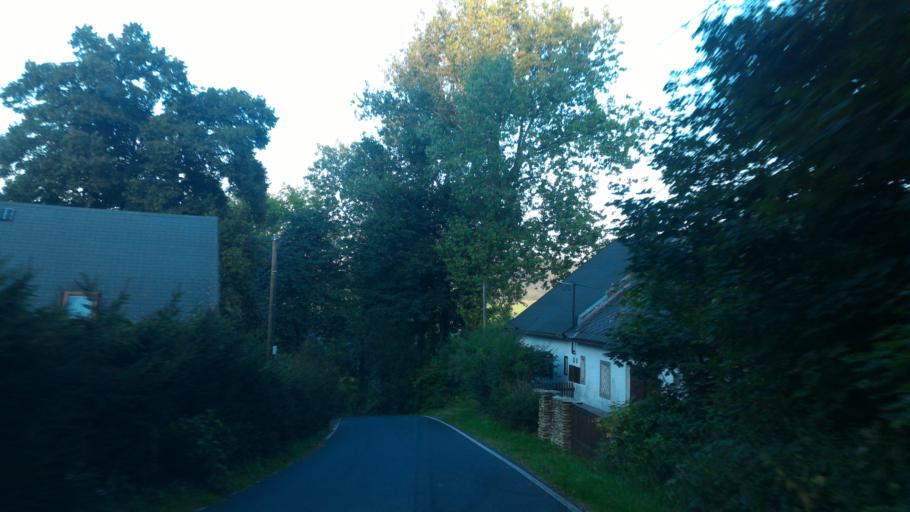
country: DE
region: Saxony
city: Kurort Jonsdorf
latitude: 50.8334
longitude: 14.6555
